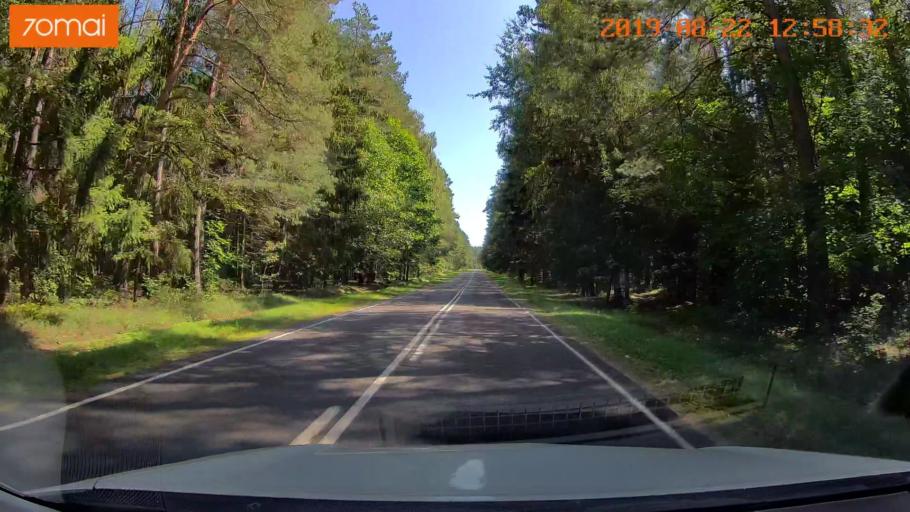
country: BY
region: Minsk
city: Prawdzinski
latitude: 53.4236
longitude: 27.7726
